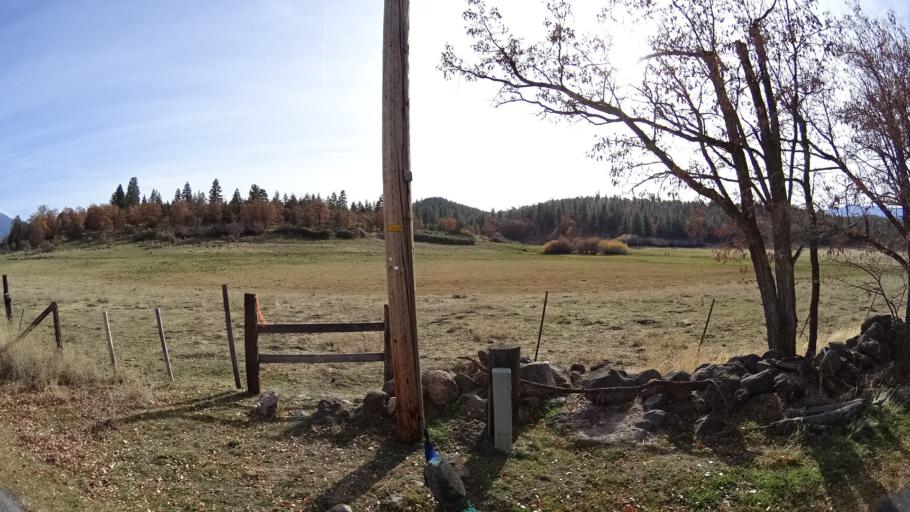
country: US
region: California
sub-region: Siskiyou County
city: Weed
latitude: 41.4651
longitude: -122.3968
